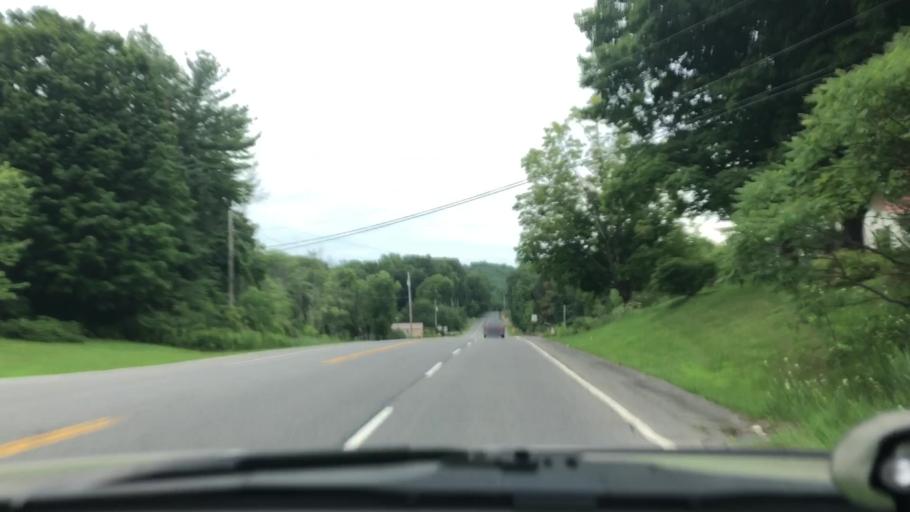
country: US
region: New York
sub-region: Saratoga County
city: Corinth
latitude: 43.1824
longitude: -73.7504
